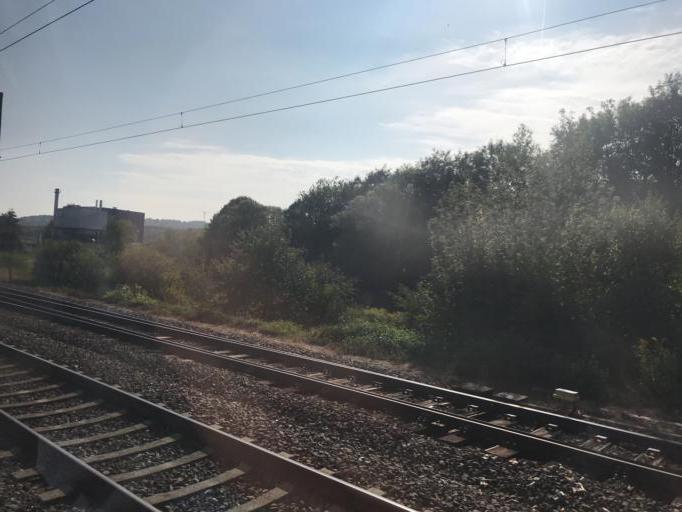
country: DE
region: Rheinland-Pfalz
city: Ellweiler
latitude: 49.6033
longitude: 7.1680
